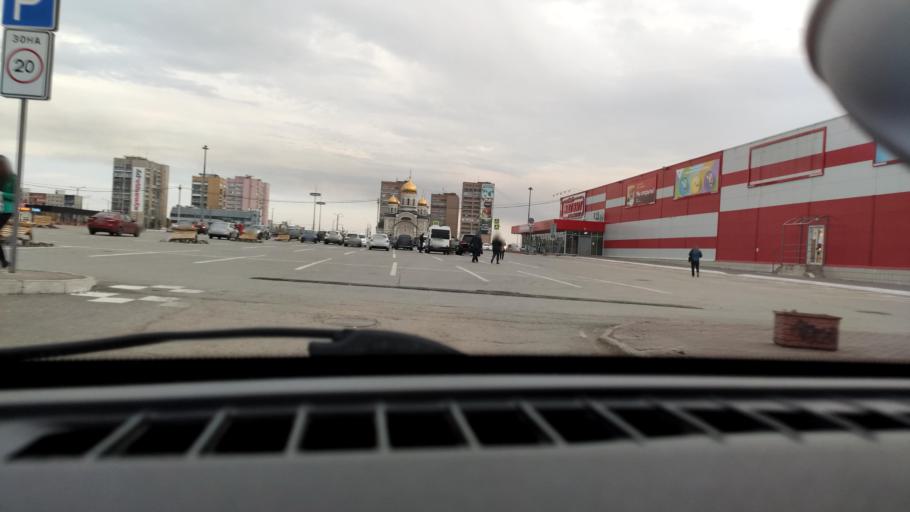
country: RU
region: Samara
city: Samara
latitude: 53.2530
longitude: 50.2181
